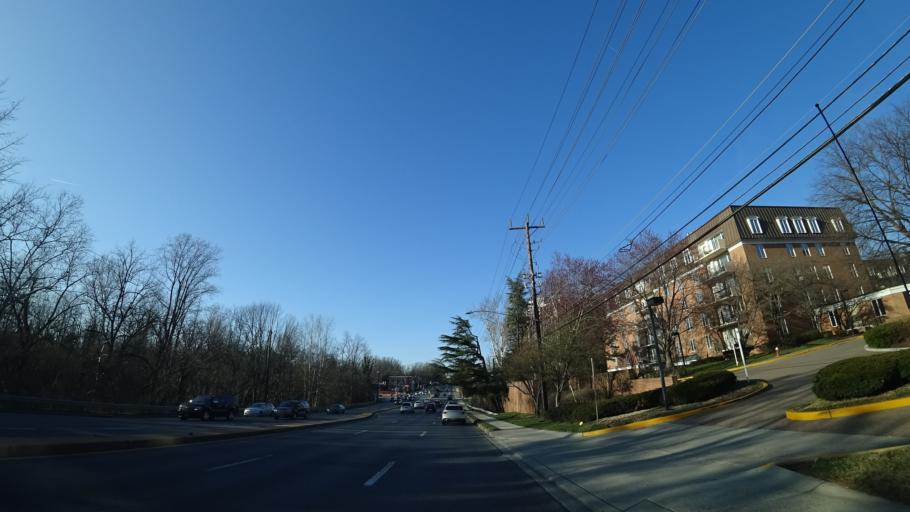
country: US
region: Maryland
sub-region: Montgomery County
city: Chevy Chase
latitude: 38.9925
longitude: -77.0771
